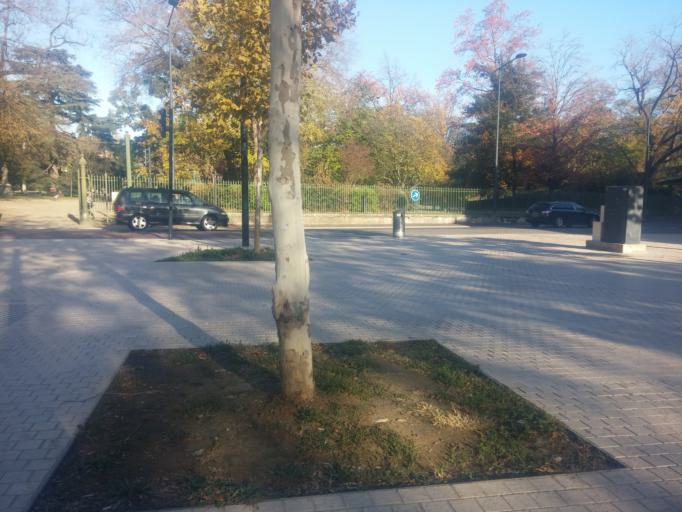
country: FR
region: Midi-Pyrenees
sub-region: Departement de la Haute-Garonne
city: Toulouse
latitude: 43.5952
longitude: 1.4512
